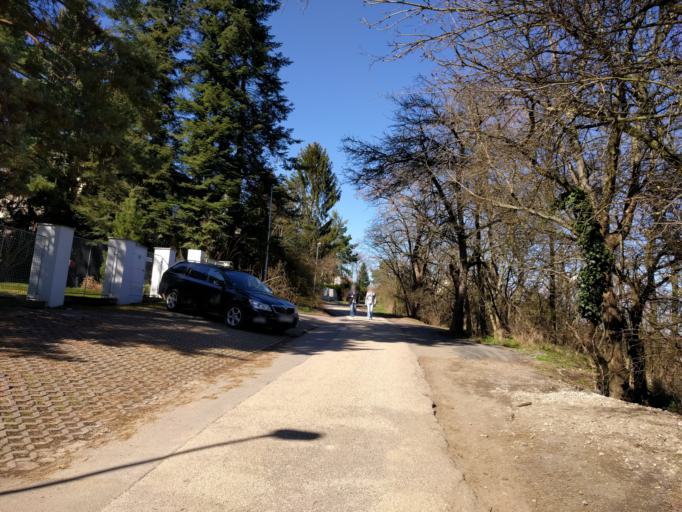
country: CZ
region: Praha
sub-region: Praha 1
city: Mala Strana
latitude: 50.1157
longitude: 14.3888
